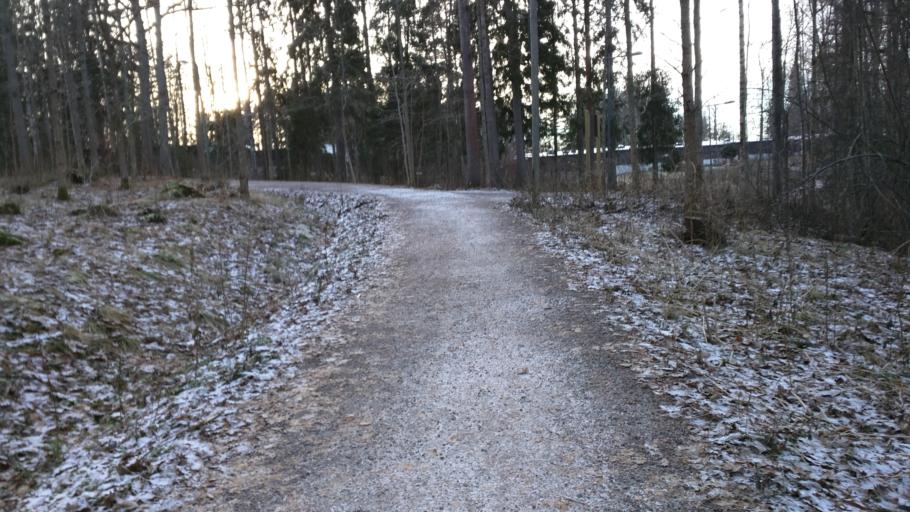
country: FI
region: Uusimaa
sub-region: Helsinki
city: Kauniainen
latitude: 60.2456
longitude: 24.7388
